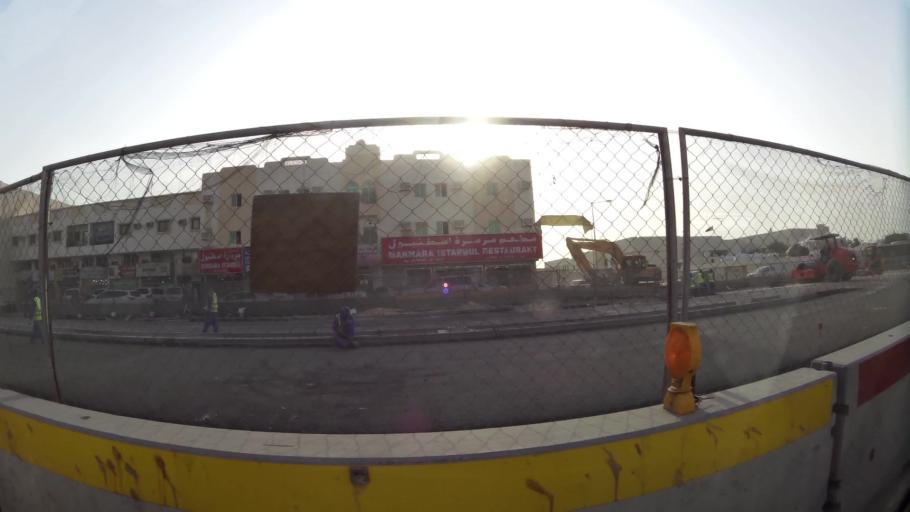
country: QA
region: Baladiyat ar Rayyan
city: Ar Rayyan
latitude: 25.2519
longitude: 51.4510
